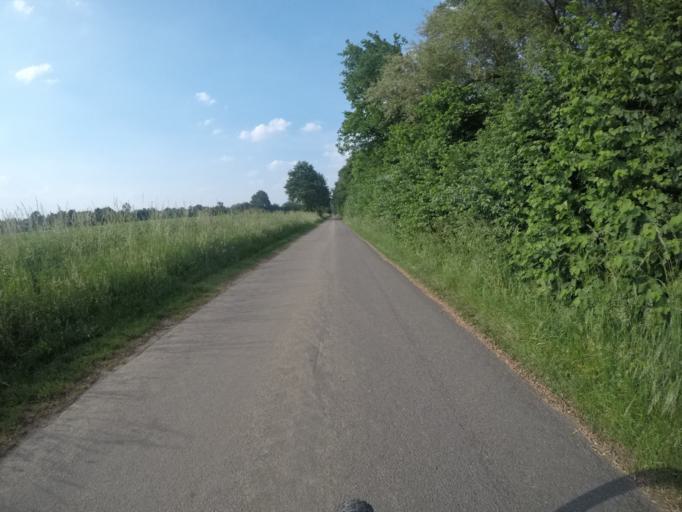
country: DE
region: North Rhine-Westphalia
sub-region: Regierungsbezirk Munster
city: Isselburg
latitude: 51.8289
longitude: 6.5081
